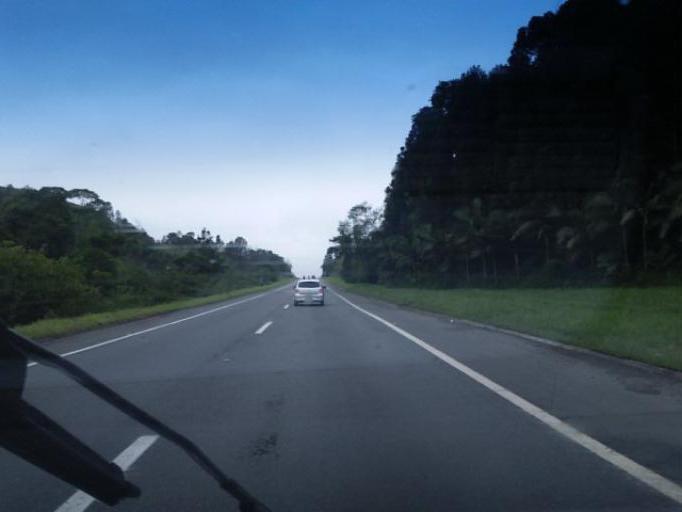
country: BR
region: Sao Paulo
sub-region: Cajati
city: Cajati
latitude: -24.9760
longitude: -48.4963
